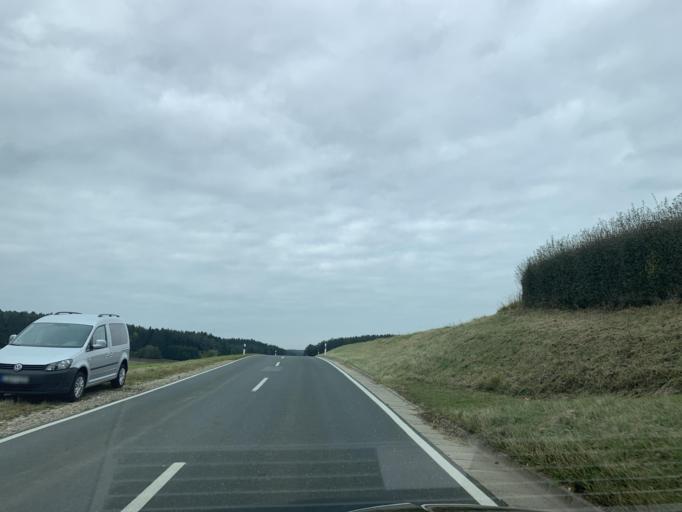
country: DE
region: Bavaria
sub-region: Upper Franconia
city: Pottenstein
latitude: 49.7282
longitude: 11.4579
